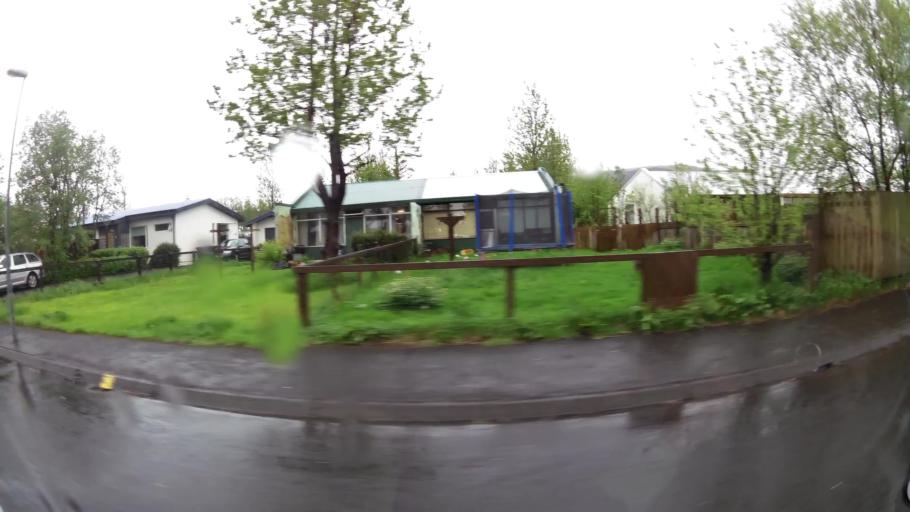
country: IS
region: South
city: Hveragerdi
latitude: 64.0005
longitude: -21.1953
